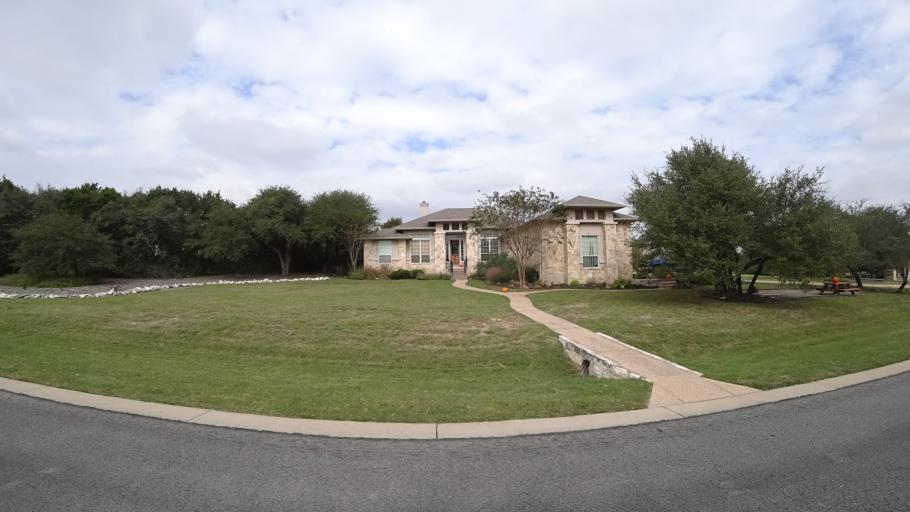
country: US
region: Texas
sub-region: Travis County
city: Shady Hollow
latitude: 30.2194
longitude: -97.8900
